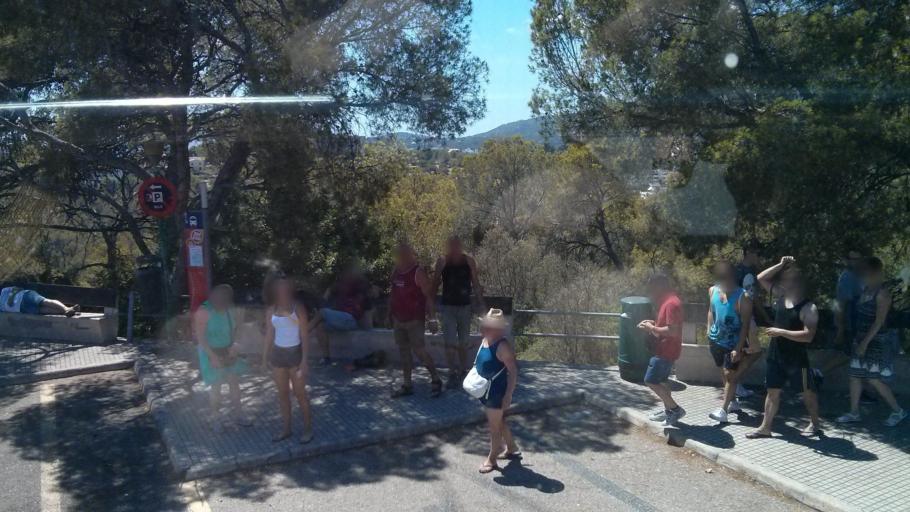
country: ES
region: Balearic Islands
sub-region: Illes Balears
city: Palma
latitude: 39.5627
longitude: 2.6192
